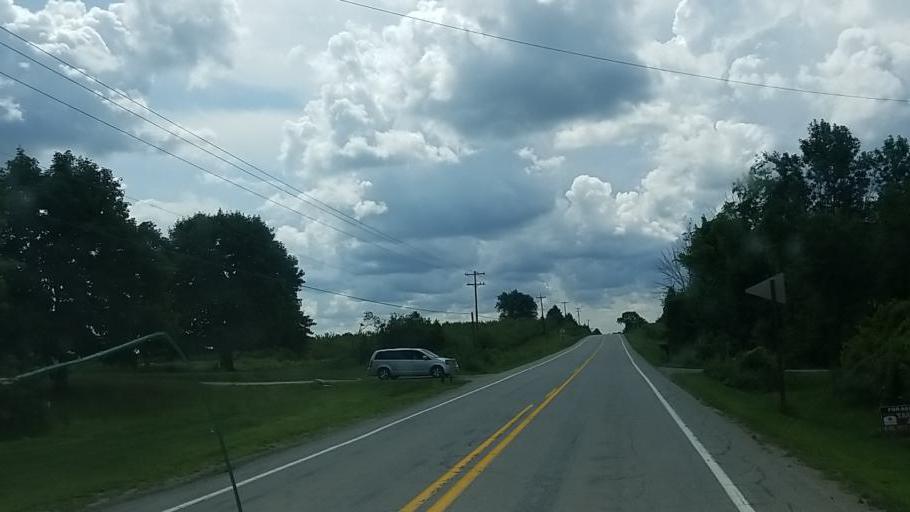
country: US
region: Michigan
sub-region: Kent County
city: Walker
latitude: 43.0877
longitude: -85.7682
